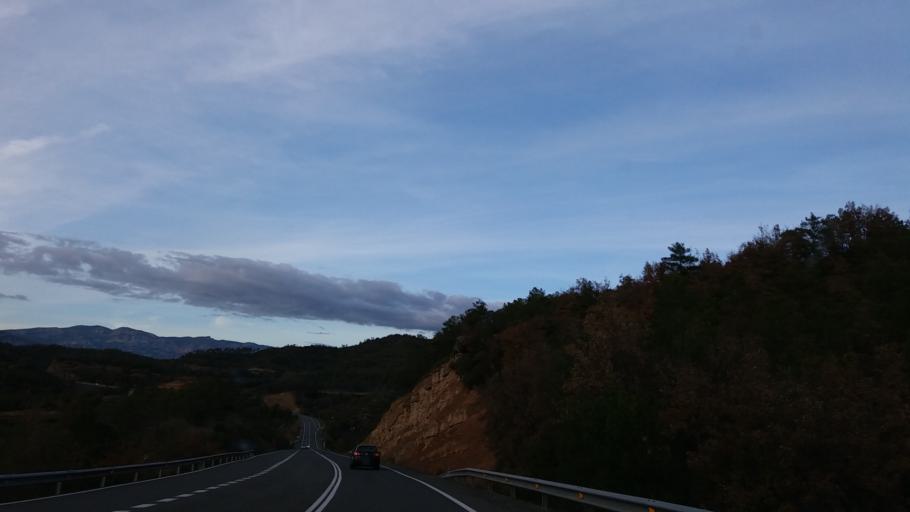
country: ES
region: Catalonia
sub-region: Provincia de Lleida
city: Tiurana
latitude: 41.9690
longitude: 1.2973
